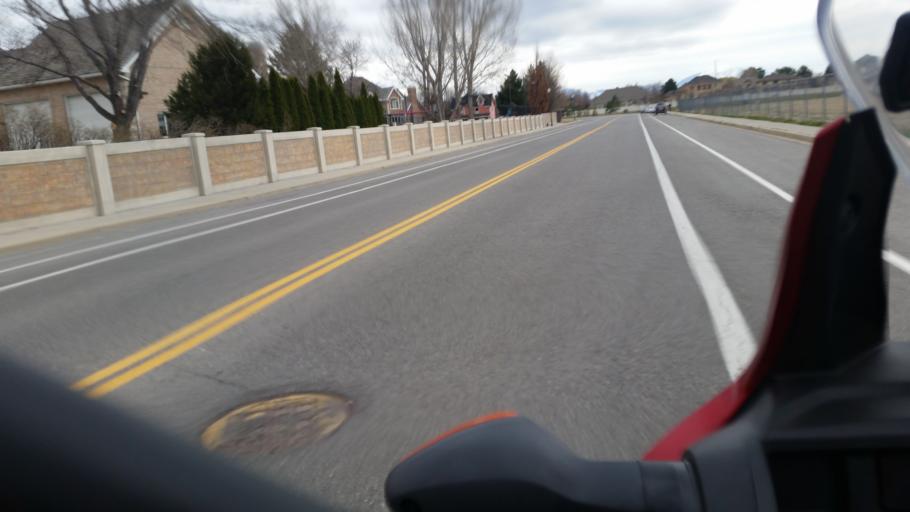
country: US
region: Utah
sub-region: Utah County
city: Orem
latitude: 40.3229
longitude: -111.6881
